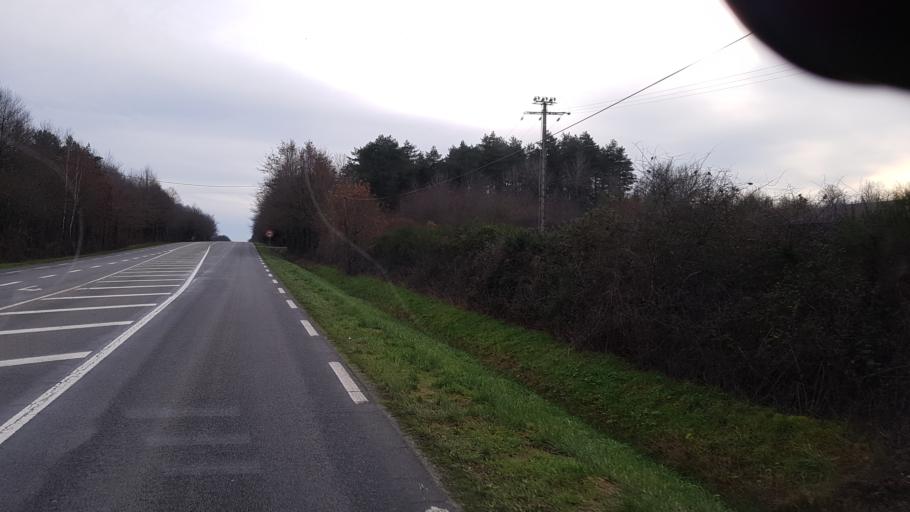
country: FR
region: Centre
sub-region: Departement du Loir-et-Cher
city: Lamotte-Beuvron
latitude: 47.5727
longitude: 2.0287
